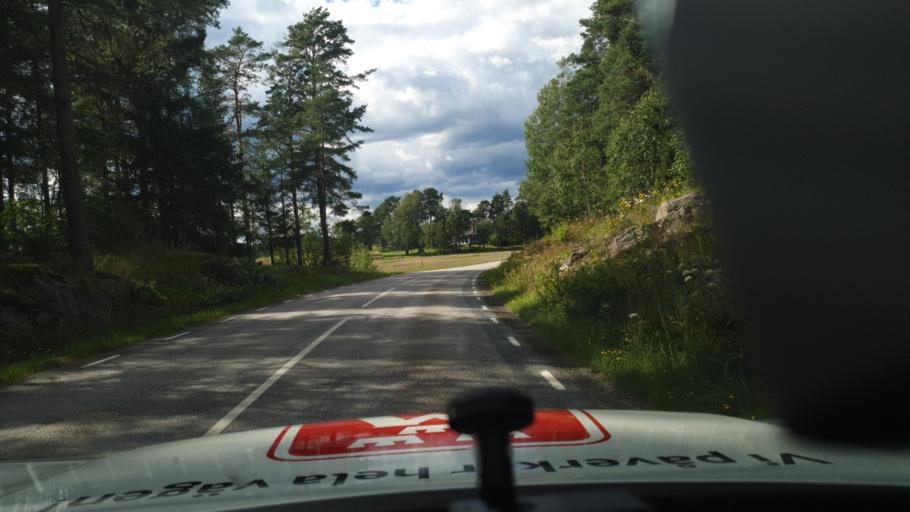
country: SE
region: Vaermland
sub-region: Saffle Kommun
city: Saeffle
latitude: 59.0802
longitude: 12.9587
